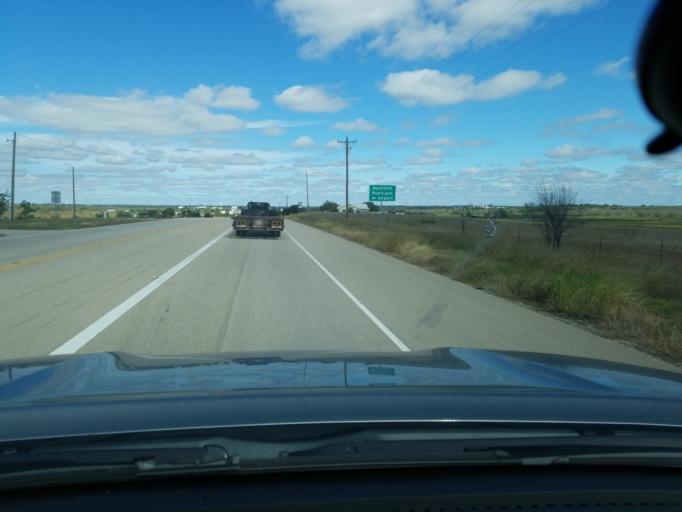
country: US
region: Texas
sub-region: Hamilton County
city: Hamilton
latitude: 31.6705
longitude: -98.1377
